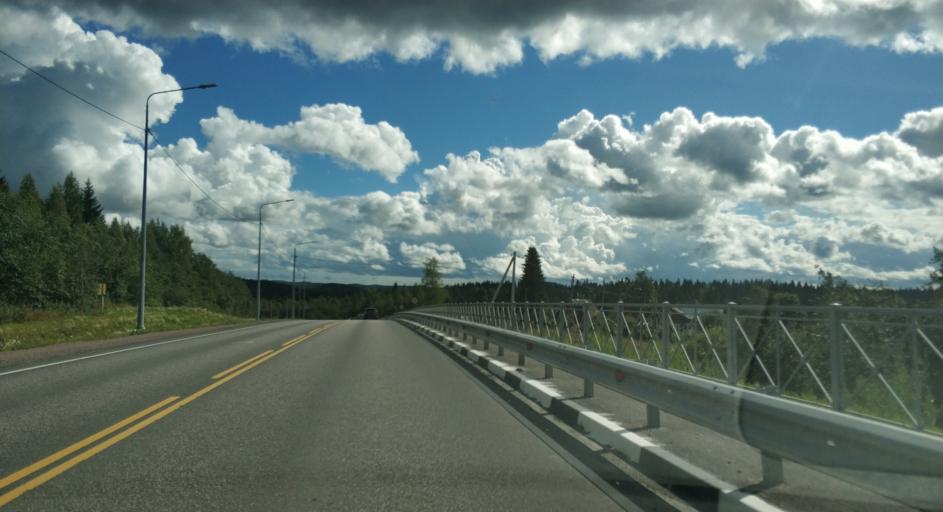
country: RU
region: Republic of Karelia
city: Ruskeala
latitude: 61.9234
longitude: 30.6072
